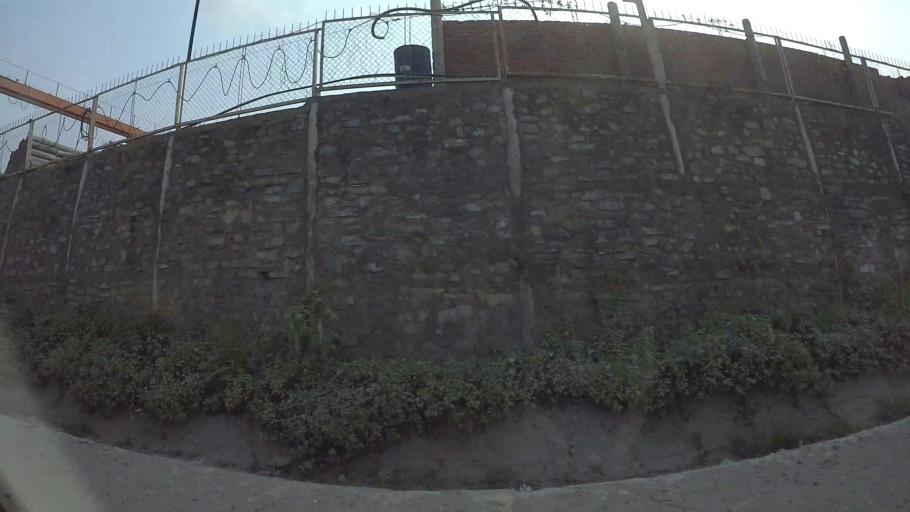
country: VN
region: Da Nang
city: Lien Chieu
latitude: 16.0385
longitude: 108.1722
